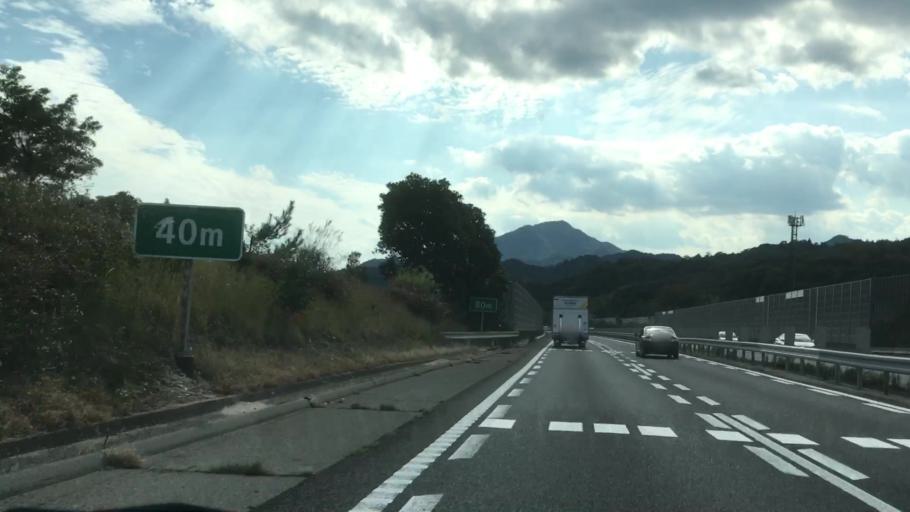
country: JP
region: Hiroshima
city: Miyajima
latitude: 34.3223
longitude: 132.2872
